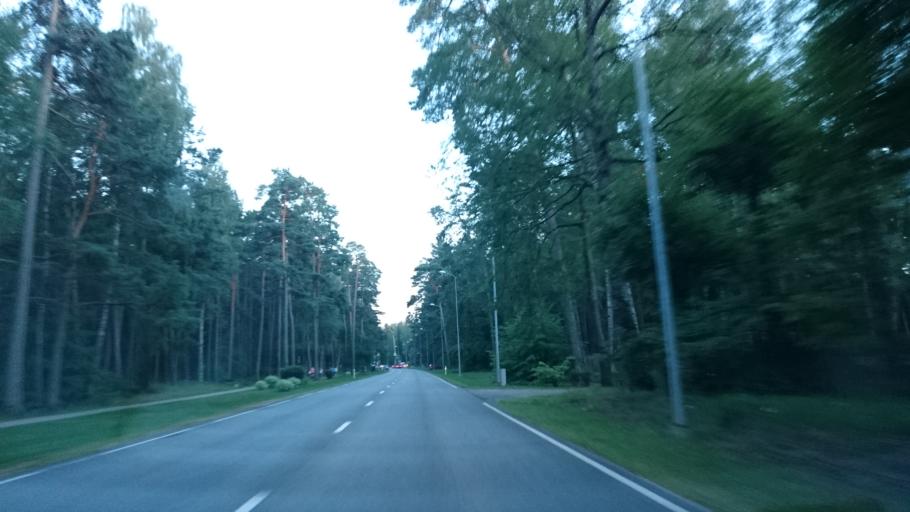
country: LV
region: Saulkrastu
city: Saulkrasti
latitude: 57.2697
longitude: 24.4147
